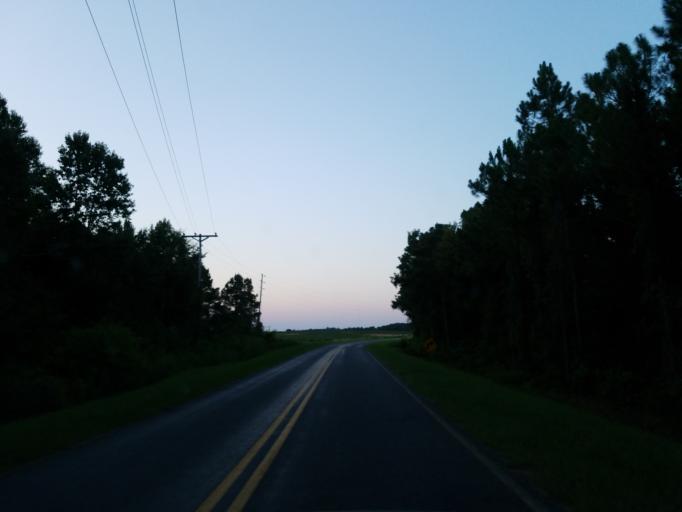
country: US
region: Georgia
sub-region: Dooly County
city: Vienna
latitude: 32.1704
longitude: -83.7986
